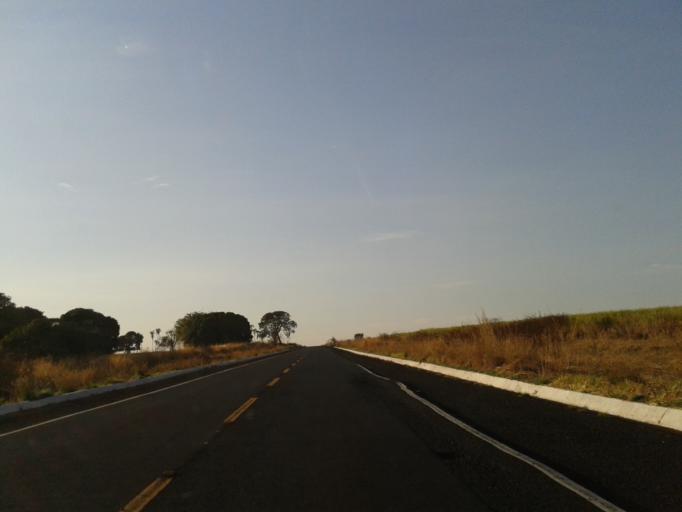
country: BR
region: Minas Gerais
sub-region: Santa Vitoria
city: Santa Vitoria
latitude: -19.1154
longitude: -50.3116
